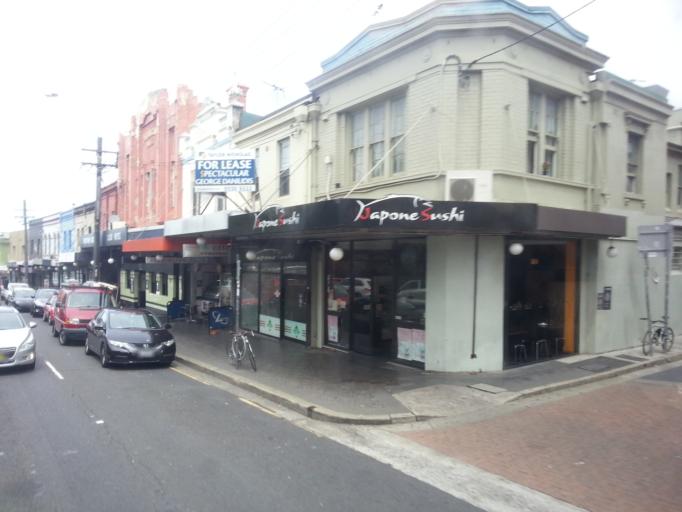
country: AU
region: New South Wales
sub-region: Marrickville
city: Newtown
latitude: -33.8993
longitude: 151.1778
